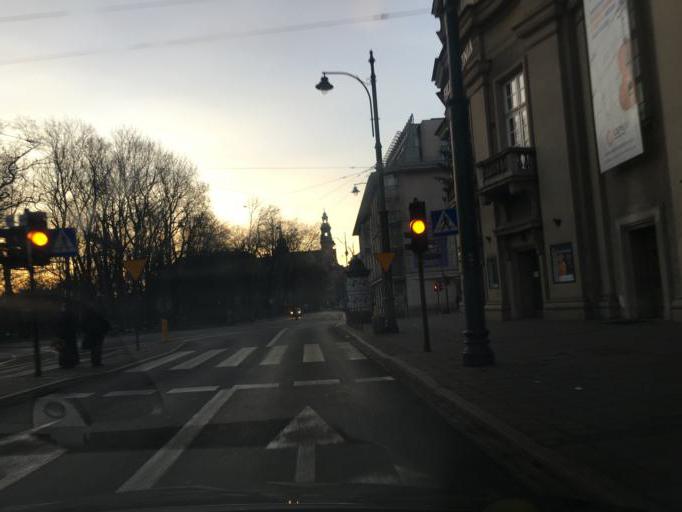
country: PL
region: Lesser Poland Voivodeship
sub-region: Krakow
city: Krakow
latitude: 50.0593
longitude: 19.9330
